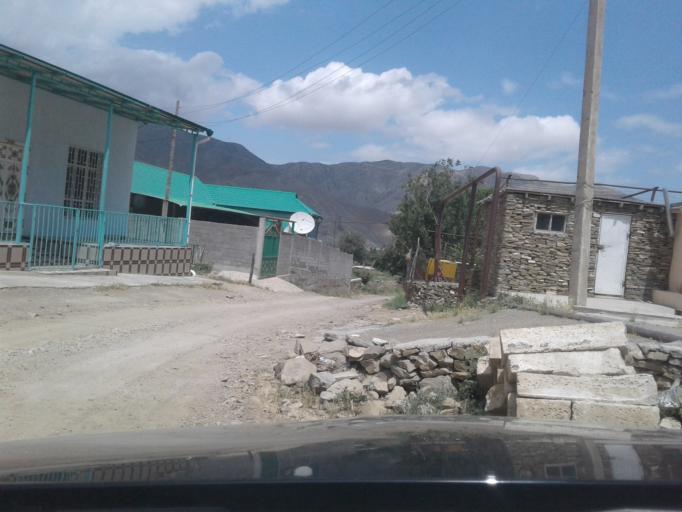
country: TM
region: Ahal
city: Baharly
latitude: 38.4720
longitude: 57.0392
